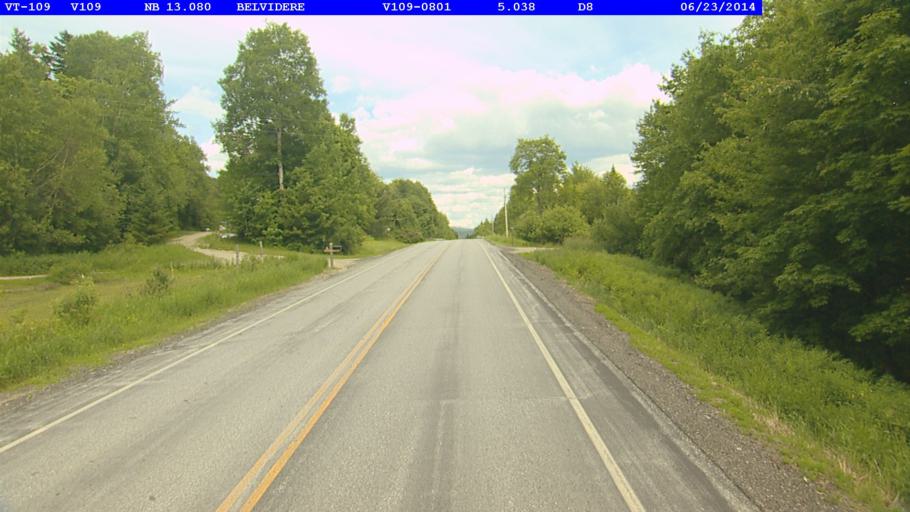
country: US
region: Vermont
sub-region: Lamoille County
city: Johnson
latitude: 44.7610
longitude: -72.6563
